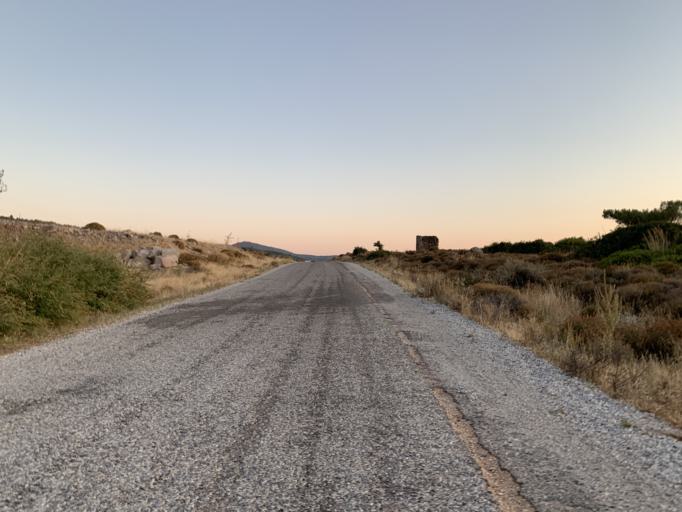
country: TR
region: Izmir
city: Uzunkuyu
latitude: 38.3285
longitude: 26.5840
